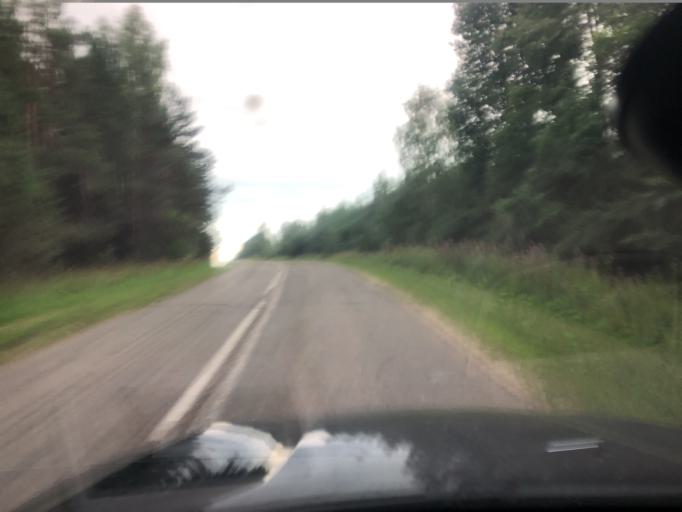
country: RU
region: Jaroslavl
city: Pereslavl'-Zalesskiy
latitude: 57.0340
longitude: 38.9085
